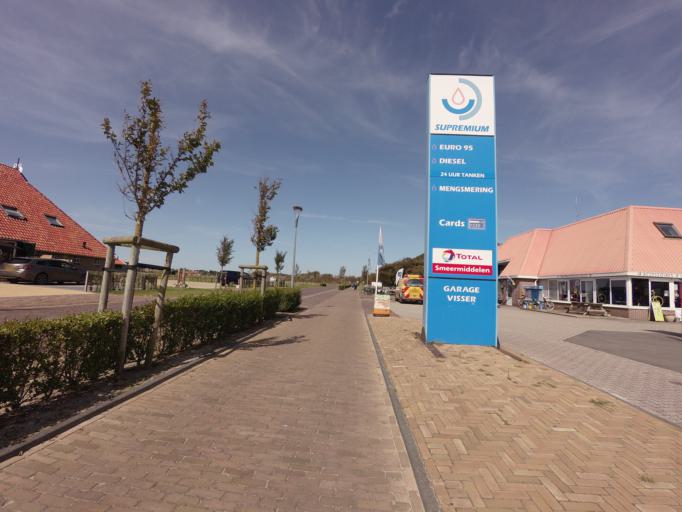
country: NL
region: Friesland
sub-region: Gemeente Ameland
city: Hollum
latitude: 53.4442
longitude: 5.6352
